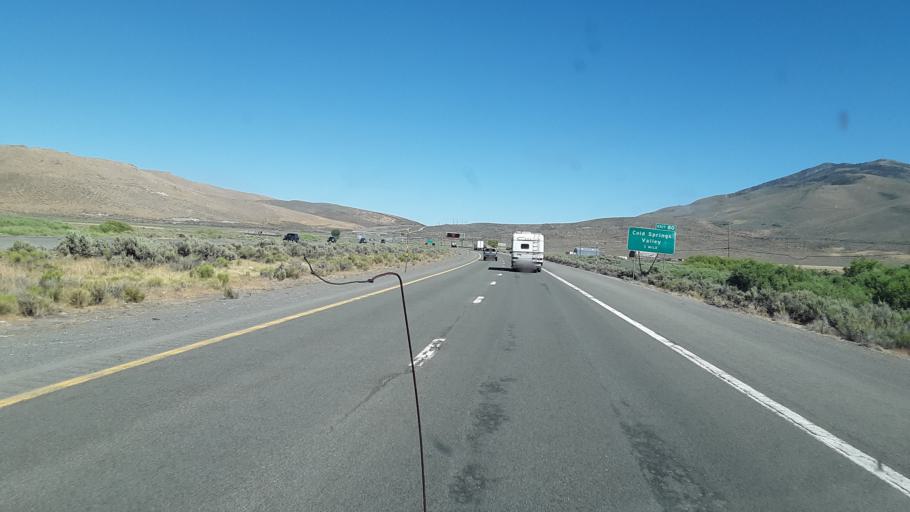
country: US
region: Nevada
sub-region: Washoe County
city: Cold Springs
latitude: 39.6518
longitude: -119.9805
